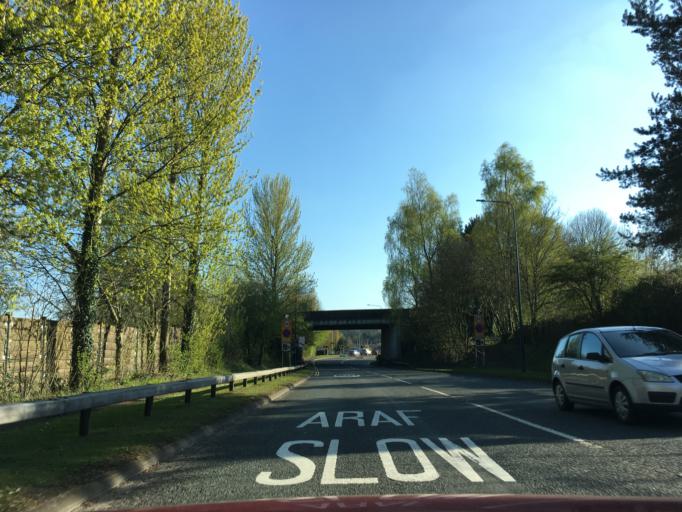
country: GB
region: Wales
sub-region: Torfaen County Borough
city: Cwmbran
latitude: 51.6577
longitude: -3.0257
